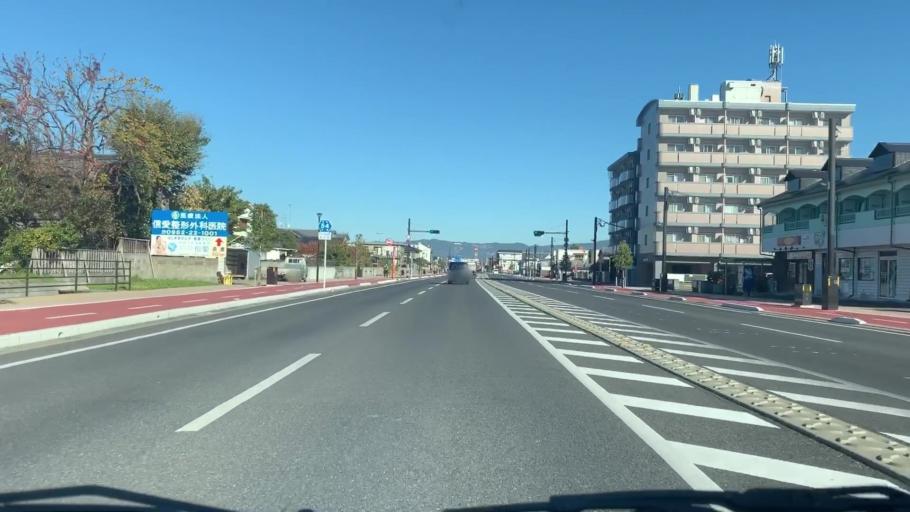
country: JP
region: Saga Prefecture
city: Saga-shi
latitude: 33.2459
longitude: 130.2931
